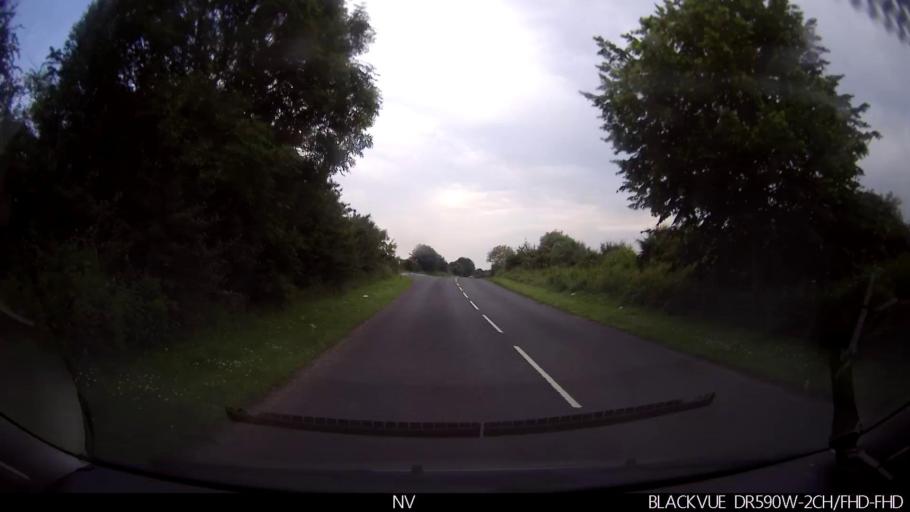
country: GB
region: England
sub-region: City of York
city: Copmanthorpe
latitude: 53.9426
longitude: -1.1421
